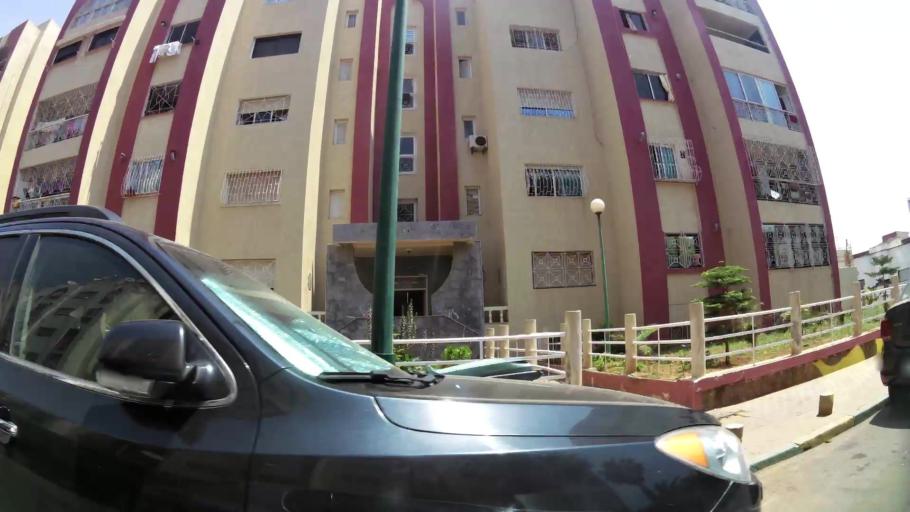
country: MA
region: Rabat-Sale-Zemmour-Zaer
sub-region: Skhirate-Temara
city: Temara
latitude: 33.9738
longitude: -6.8948
